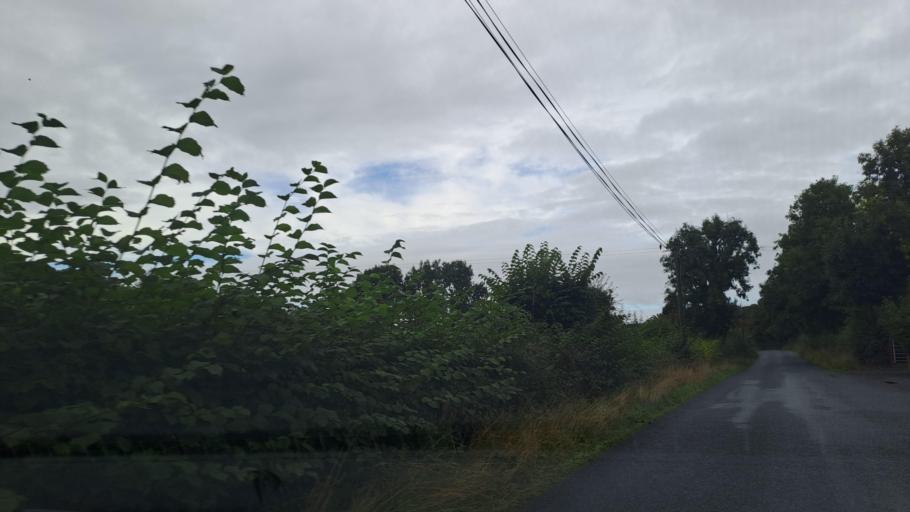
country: IE
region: Ulster
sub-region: County Monaghan
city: Carrickmacross
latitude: 53.9682
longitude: -6.7460
